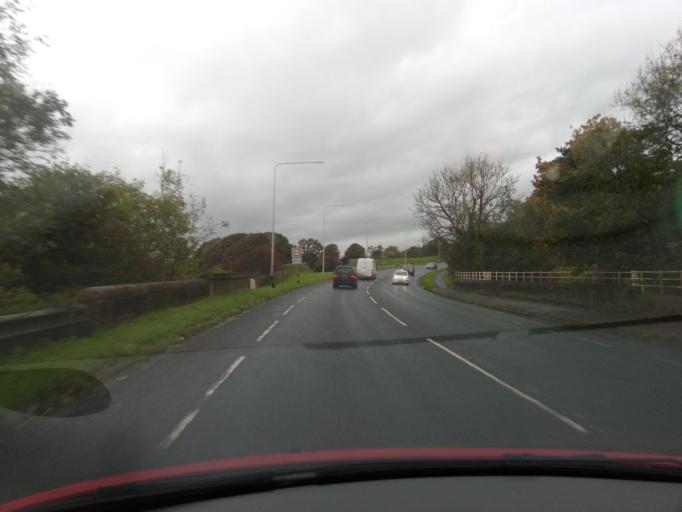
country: GB
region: England
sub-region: Lancashire
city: Preston
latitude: 53.8168
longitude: -2.7320
